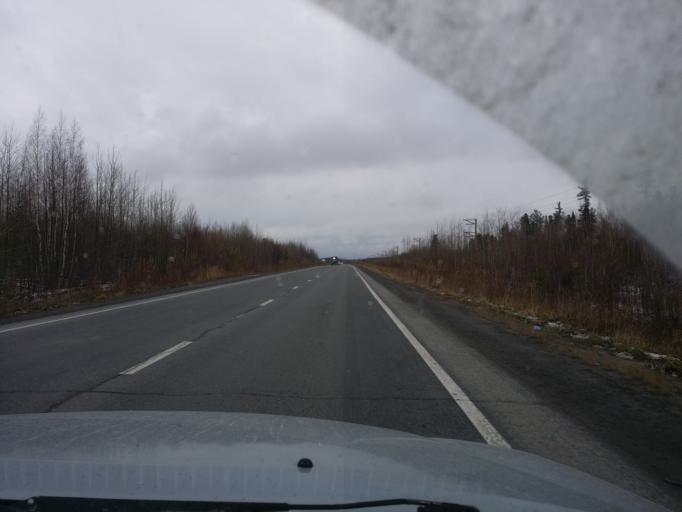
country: RU
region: Khanty-Mansiyskiy Avtonomnyy Okrug
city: Langepas
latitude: 61.3198
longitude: 75.0802
